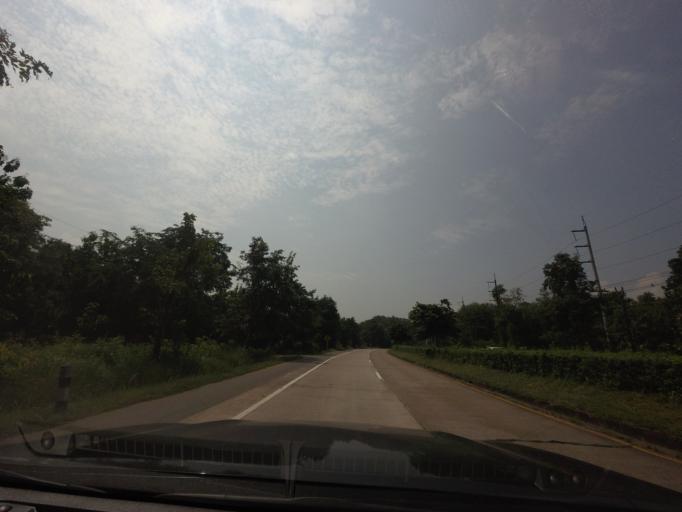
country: TH
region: Phrae
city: Sung Men
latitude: 18.0005
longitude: 100.1032
